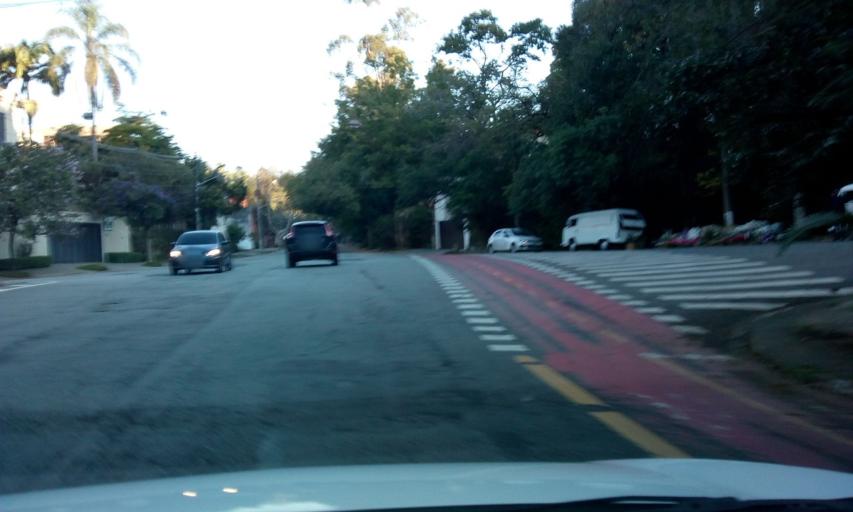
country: BR
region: Sao Paulo
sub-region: Sao Paulo
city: Sao Paulo
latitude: -23.5924
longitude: -46.7030
